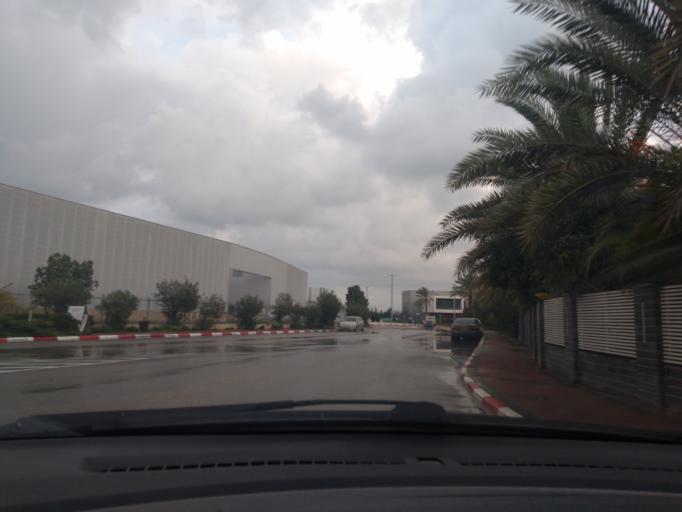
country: IL
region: Central District
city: Elyakhin
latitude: 32.4007
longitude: 34.8970
